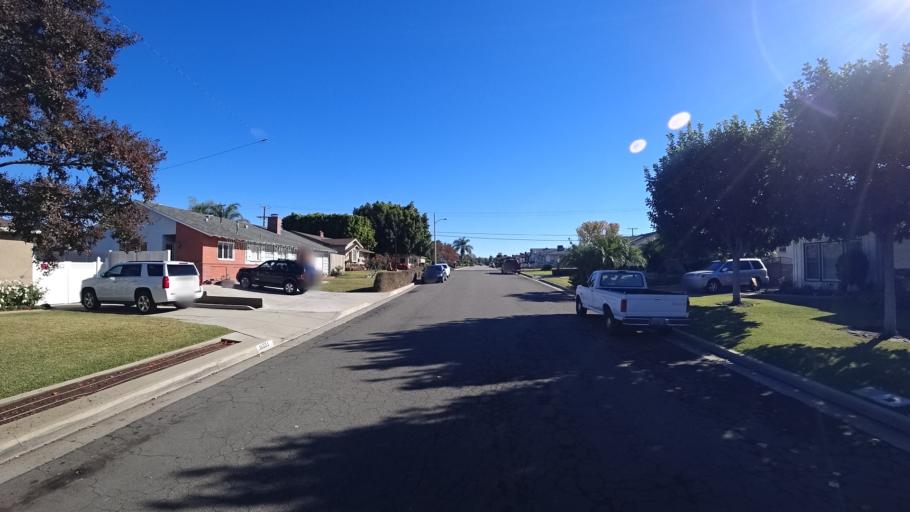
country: US
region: California
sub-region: Los Angeles County
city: East La Mirada
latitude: 33.9416
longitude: -117.9772
